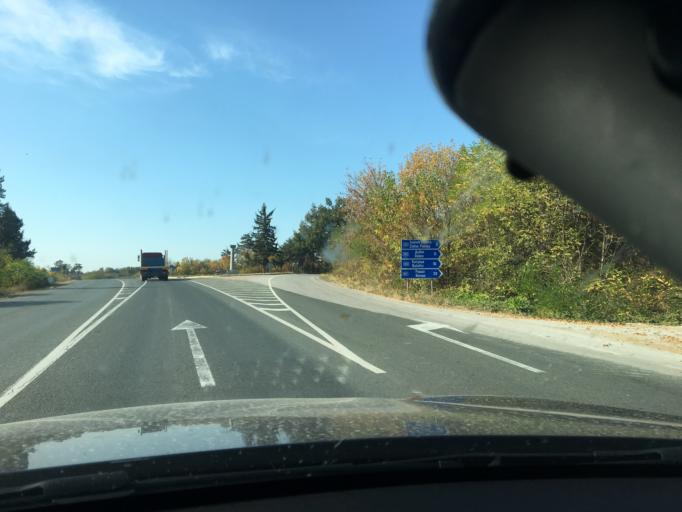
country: BG
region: Lovech
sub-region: Obshtina Yablanitsa
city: Yablanitsa
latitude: 43.0596
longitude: 24.2180
